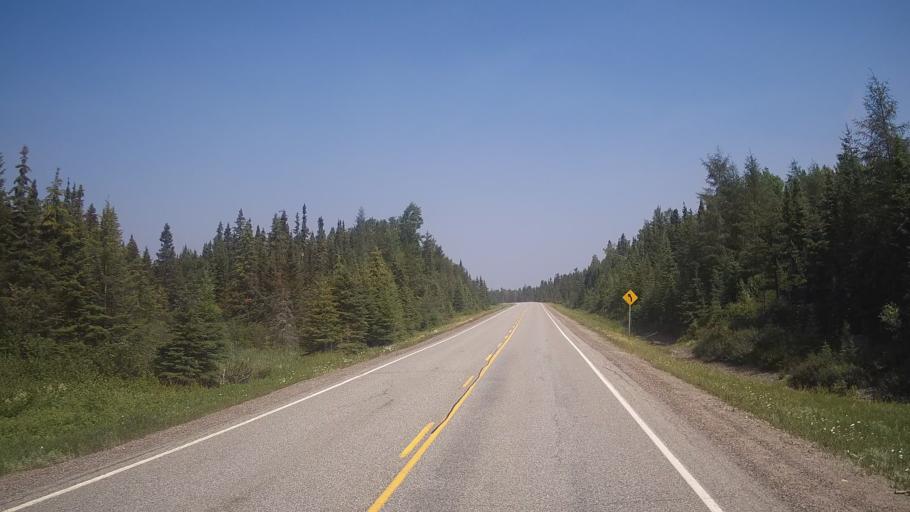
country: CA
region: Ontario
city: Timmins
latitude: 48.0963
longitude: -81.5924
